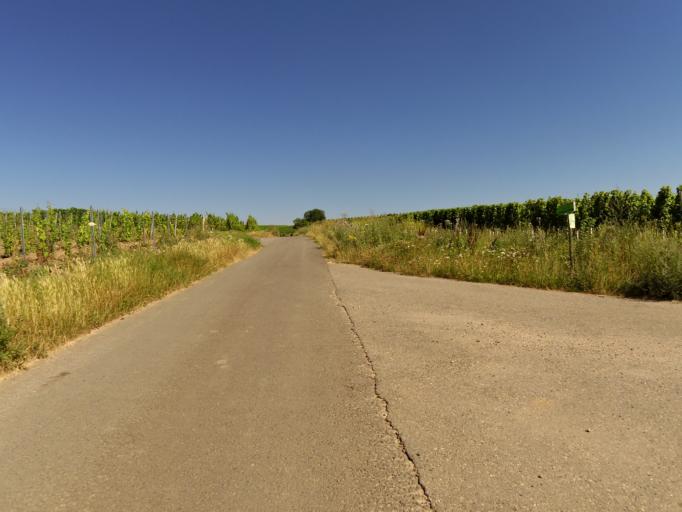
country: DE
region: Rheinland-Pfalz
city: Dackenheim
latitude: 49.5192
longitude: 8.2018
